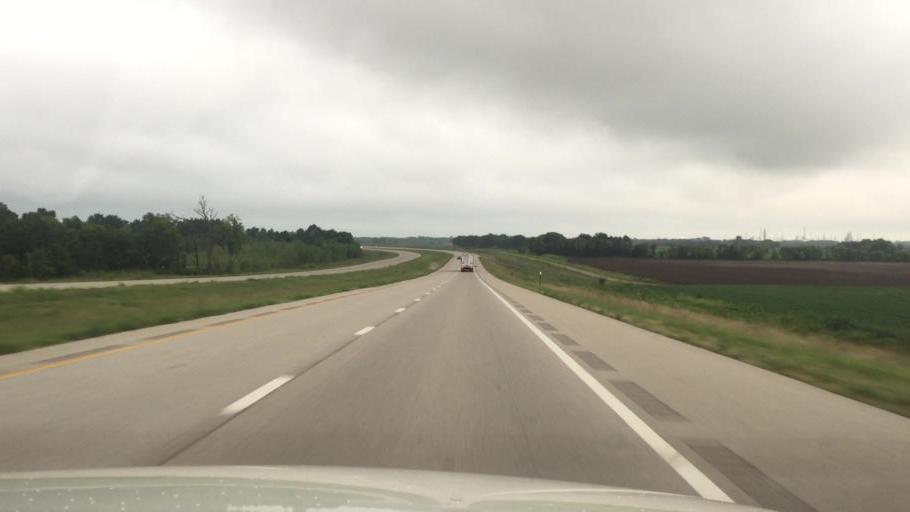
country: US
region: Kansas
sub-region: Montgomery County
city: Coffeyville
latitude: 37.0846
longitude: -95.5899
